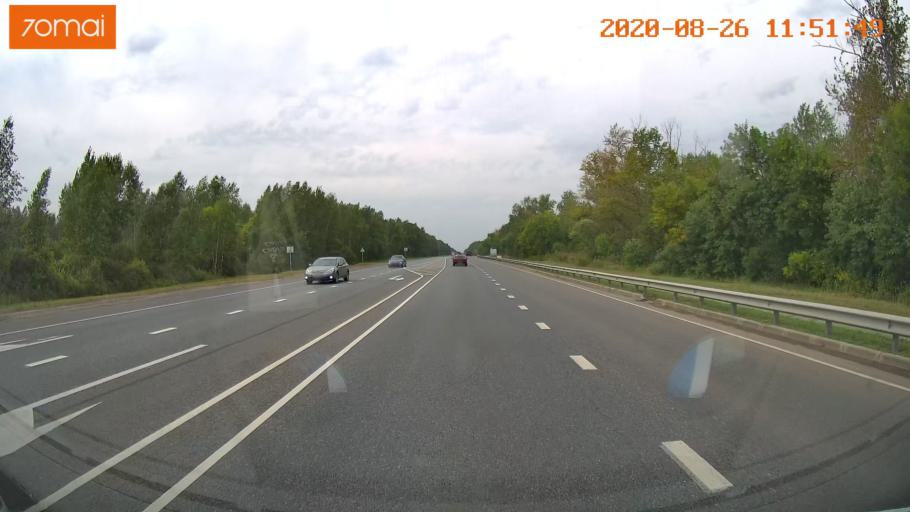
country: RU
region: Rjazan
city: Lesnoy
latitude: 54.2962
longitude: 40.4703
